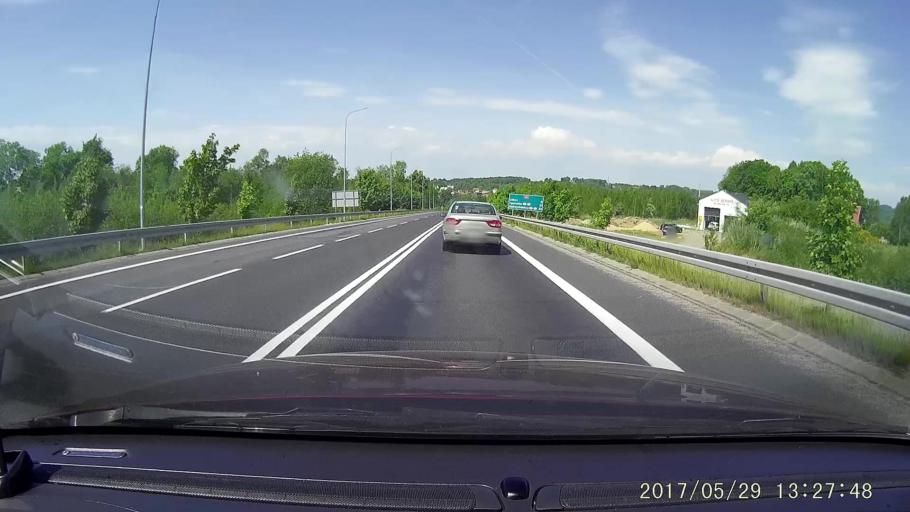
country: PL
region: Lower Silesian Voivodeship
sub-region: Powiat lubanski
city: Olszyna
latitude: 51.0584
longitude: 15.3735
